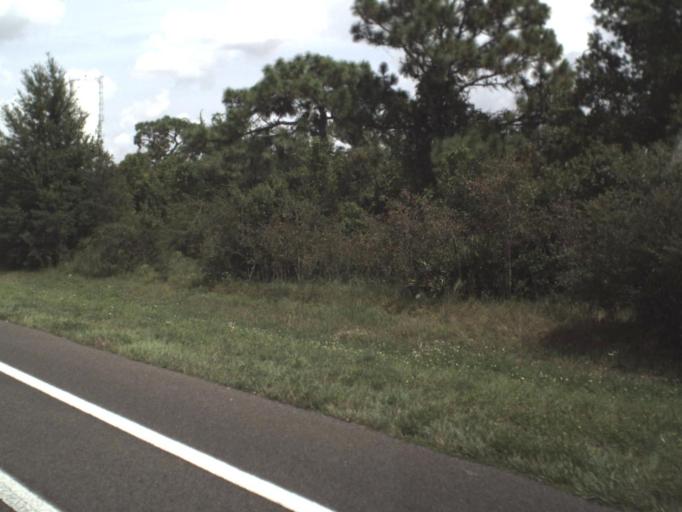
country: US
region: Florida
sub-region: Polk County
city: Crooked Lake Park
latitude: 27.8319
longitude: -81.5903
